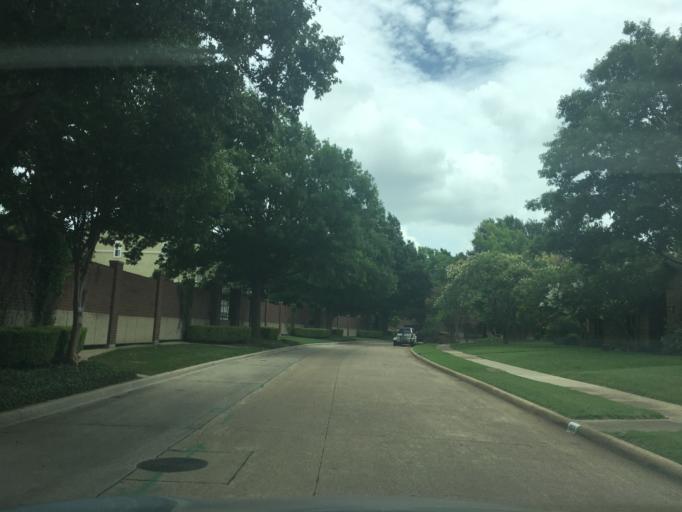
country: US
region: Texas
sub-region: Dallas County
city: Richardson
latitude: 32.9332
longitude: -96.7237
